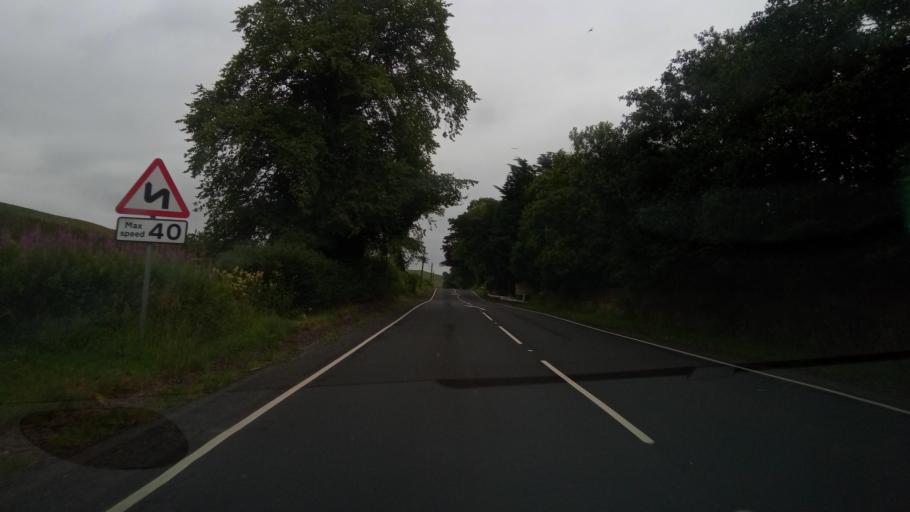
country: GB
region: Scotland
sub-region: The Scottish Borders
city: Hawick
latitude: 55.3512
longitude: -2.9172
